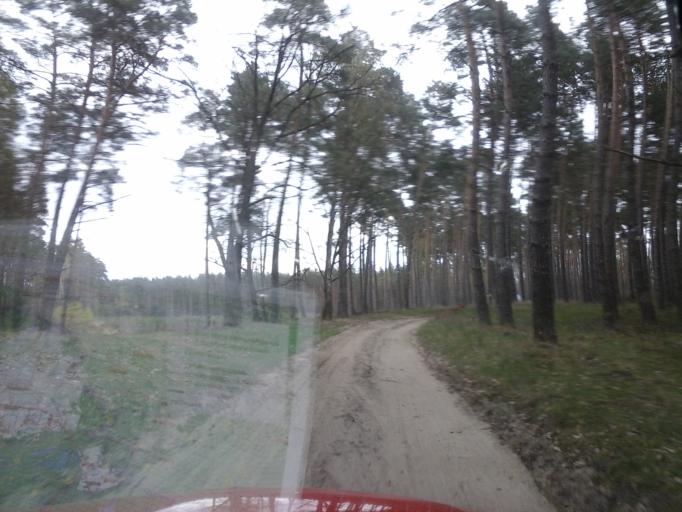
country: PL
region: West Pomeranian Voivodeship
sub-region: Powiat choszczenski
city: Bierzwnik
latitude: 53.0238
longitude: 15.5828
